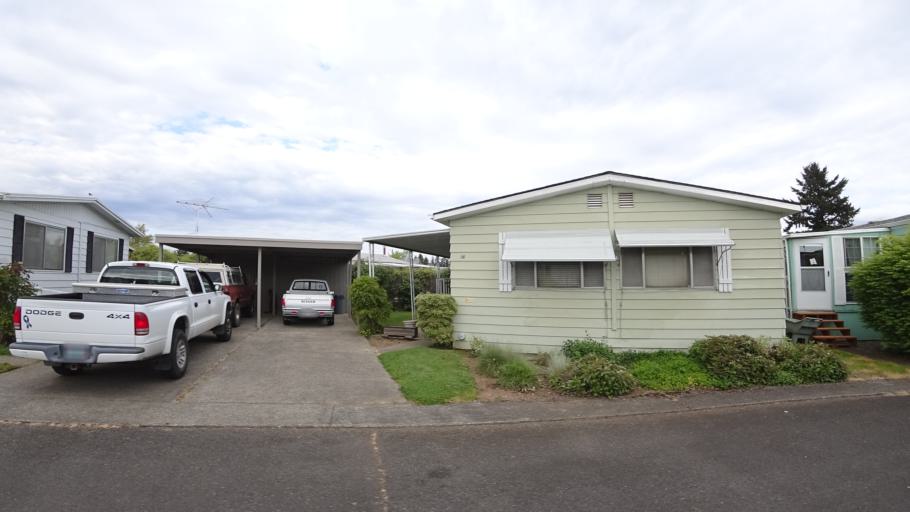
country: US
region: Oregon
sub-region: Washington County
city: Hillsboro
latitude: 45.5027
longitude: -122.9549
